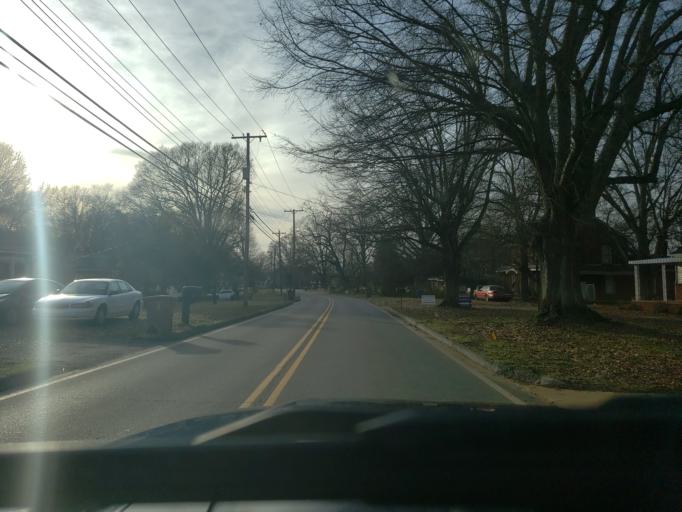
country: US
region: North Carolina
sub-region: Cleveland County
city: Shelby
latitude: 35.2799
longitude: -81.5189
